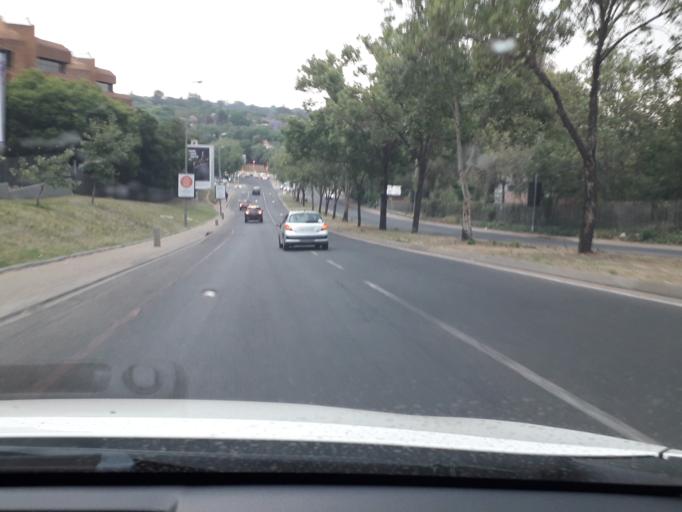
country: ZA
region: Gauteng
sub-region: City of Johannesburg Metropolitan Municipality
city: Johannesburg
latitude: -26.1027
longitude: 28.0480
